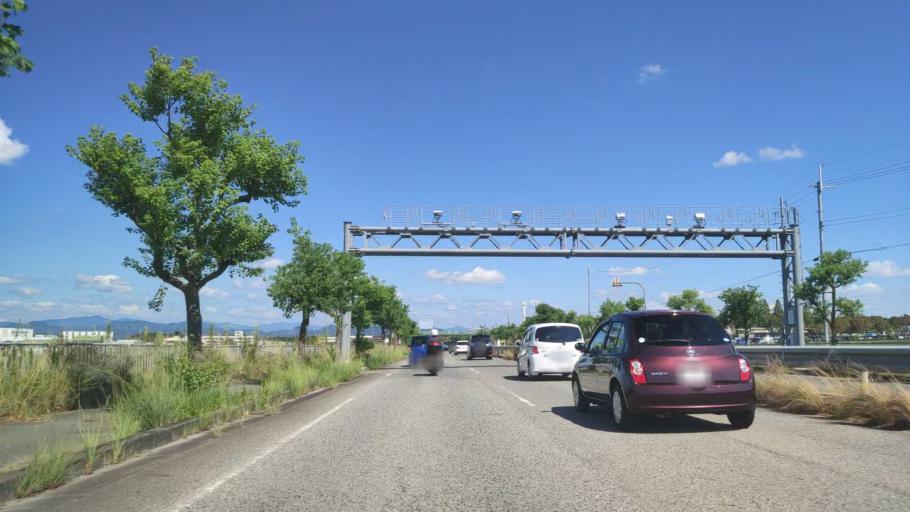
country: JP
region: Hyogo
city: Ono
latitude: 34.8661
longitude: 134.9522
